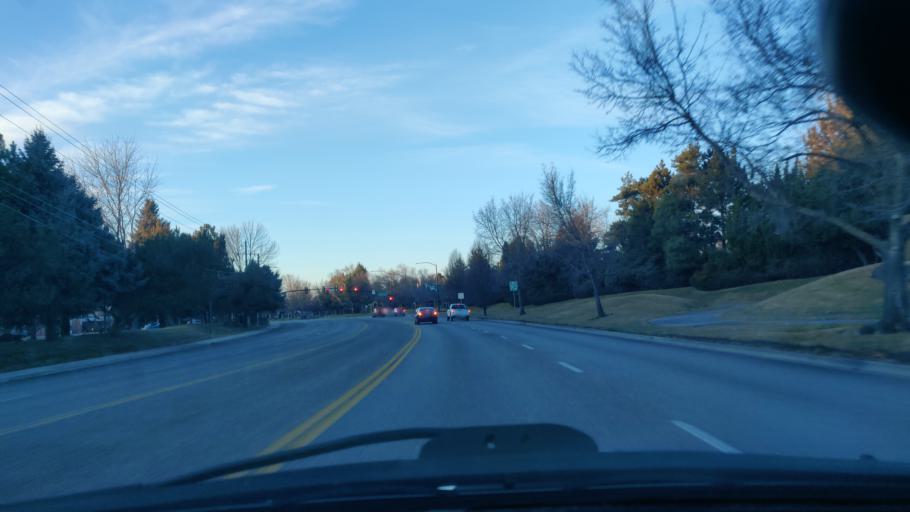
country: US
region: Idaho
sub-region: Ada County
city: Boise
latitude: 43.5881
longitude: -116.1735
